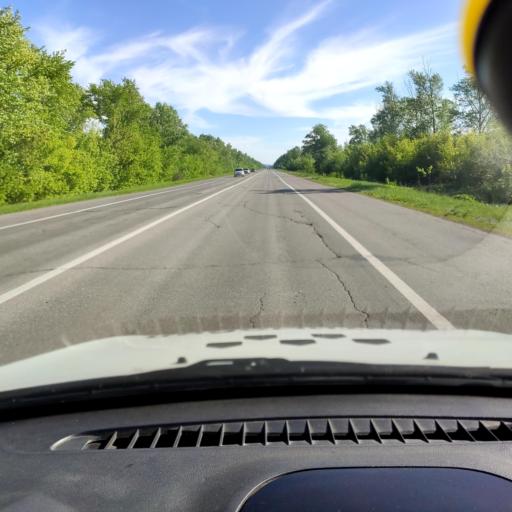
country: RU
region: Samara
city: Tol'yatti
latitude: 53.6094
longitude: 49.4114
